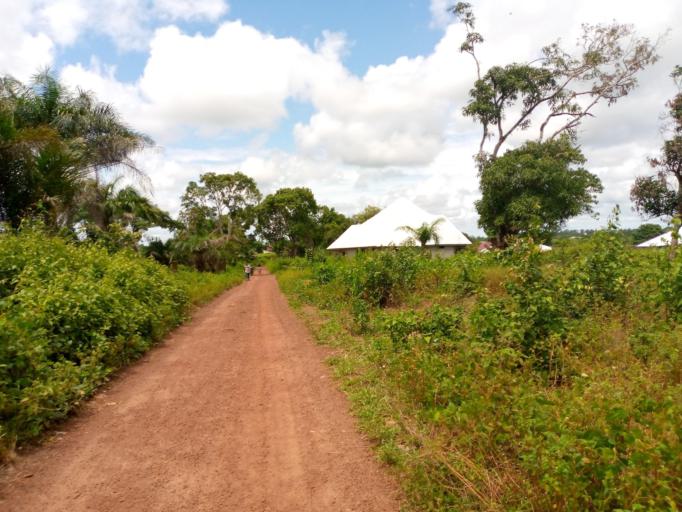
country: SL
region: Northern Province
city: Magburaka
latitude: 8.7253
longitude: -11.9233
